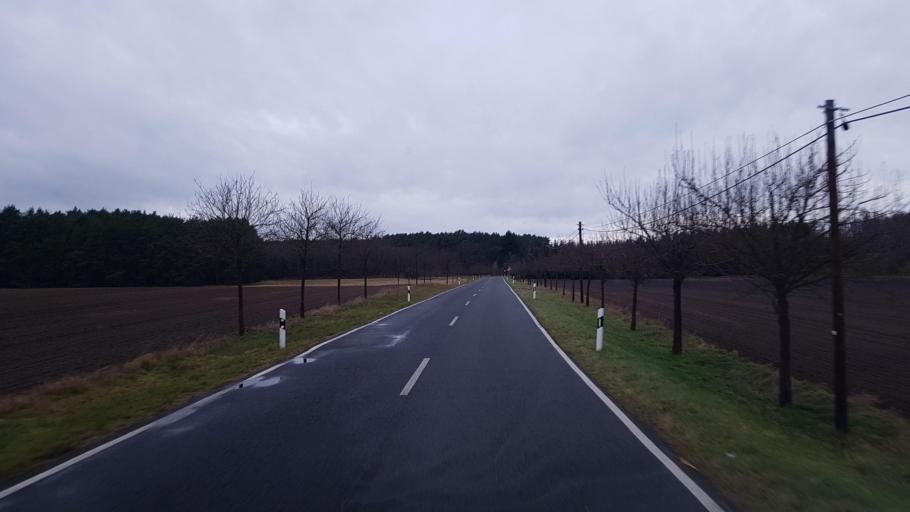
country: DE
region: Brandenburg
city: Tauche
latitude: 52.0611
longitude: 14.0995
